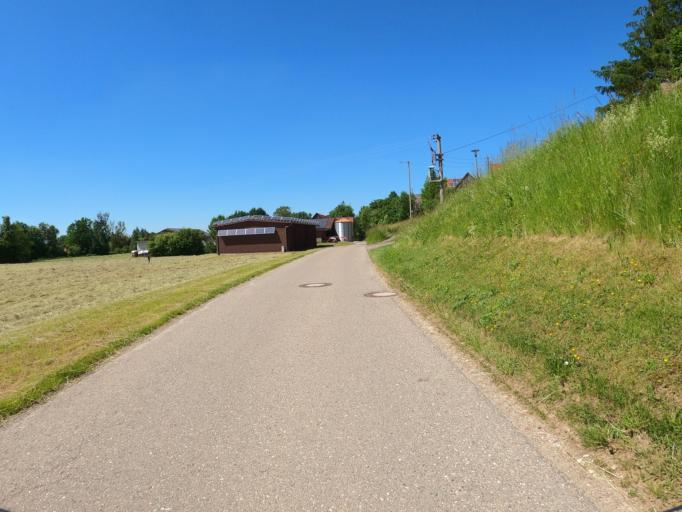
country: DE
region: Bavaria
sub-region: Swabia
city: Pfaffenhofen an der Roth
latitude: 48.3691
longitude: 10.1529
